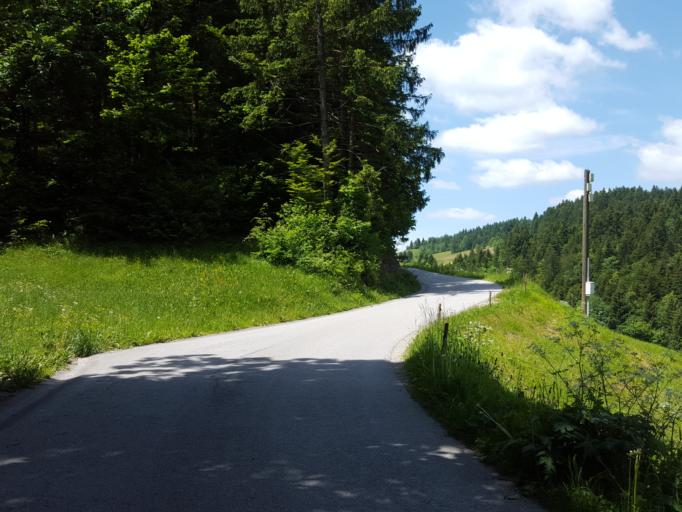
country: SI
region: Ziri
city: Ziri
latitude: 46.0067
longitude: 14.1500
